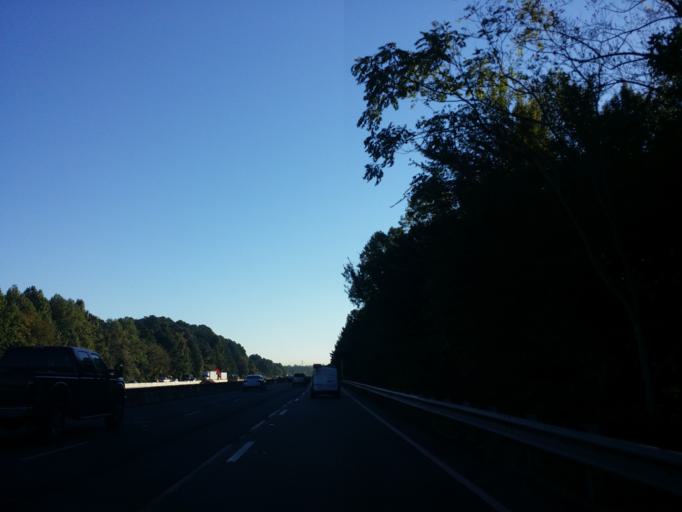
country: US
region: North Carolina
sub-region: Wake County
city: West Raleigh
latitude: 35.7542
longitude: -78.6823
